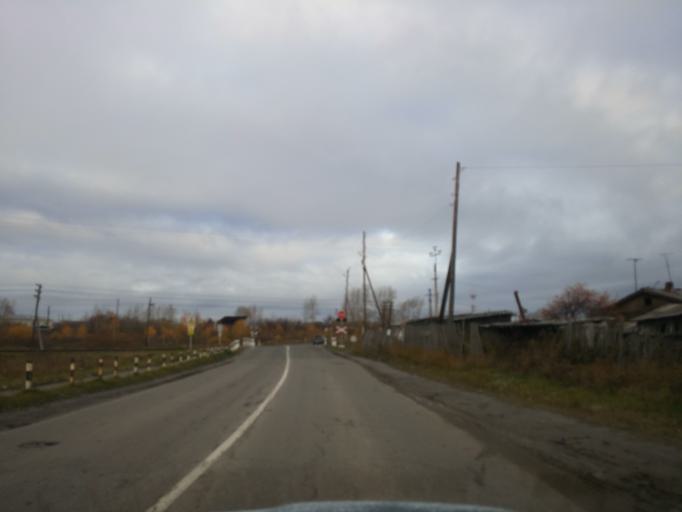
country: RU
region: Sverdlovsk
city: Turinsk
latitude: 58.0299
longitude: 63.7041
